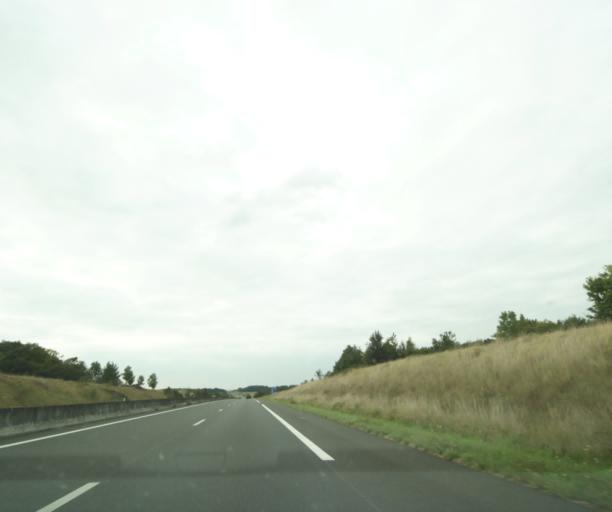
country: FR
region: Centre
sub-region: Departement d'Indre-et-Loire
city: Saint-Paterne-Racan
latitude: 47.6224
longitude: 0.5158
